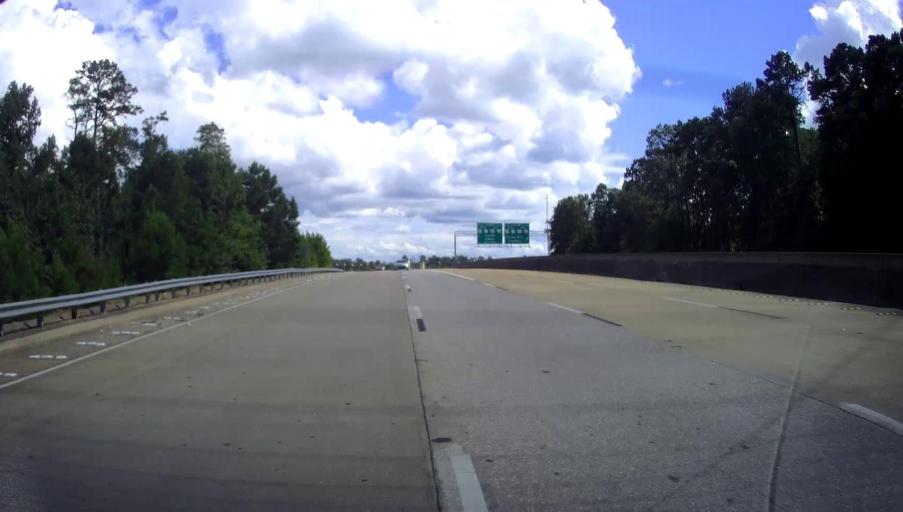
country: US
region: Georgia
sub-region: Muscogee County
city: Columbus
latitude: 32.4098
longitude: -84.9256
